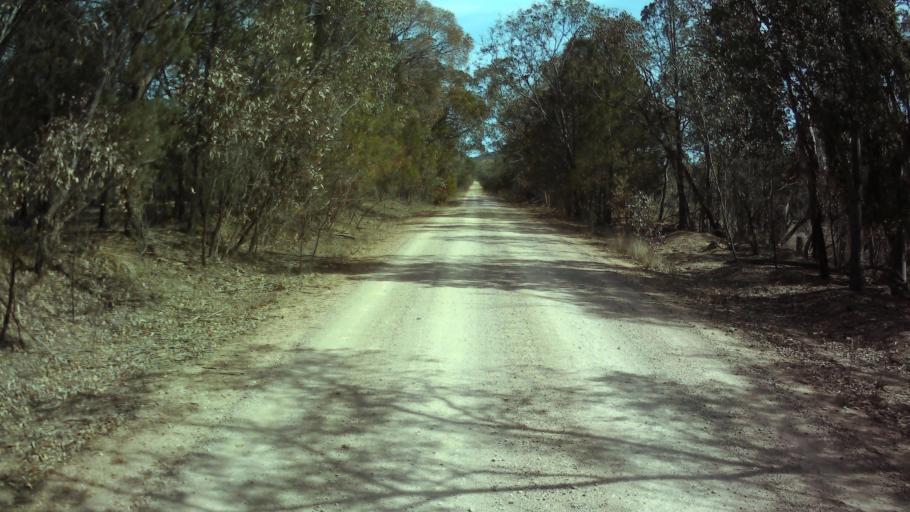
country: AU
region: New South Wales
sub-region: Weddin
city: Grenfell
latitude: -33.8798
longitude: 148.1505
